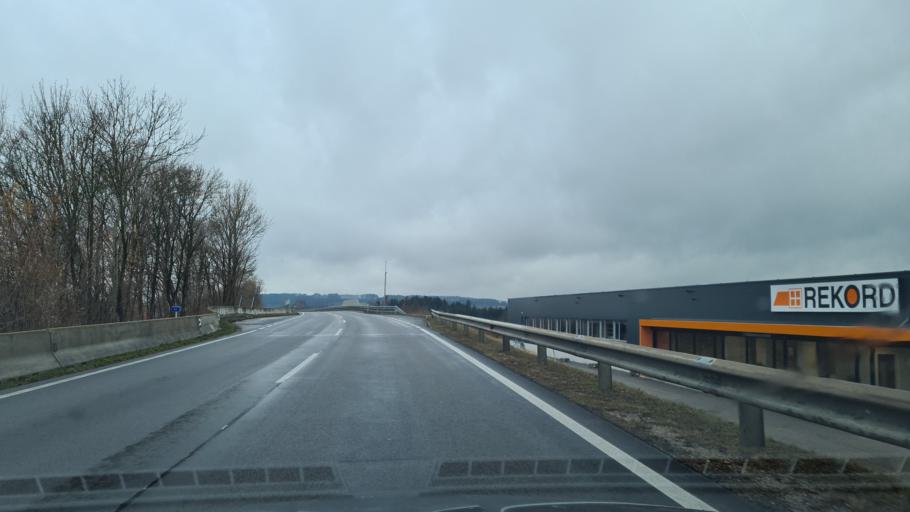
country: AT
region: Upper Austria
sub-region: Politischer Bezirk Vocklabruck
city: Oberhofen am Irrsee
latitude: 47.9593
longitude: 13.3047
